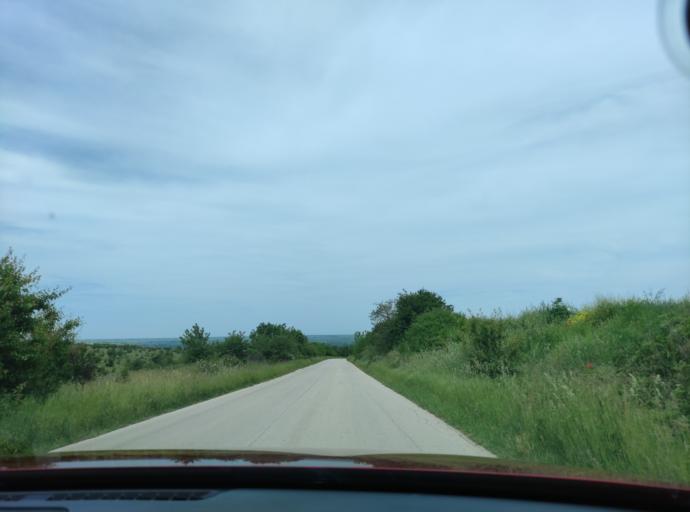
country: BG
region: Pleven
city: Iskur
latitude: 43.5309
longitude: 24.3051
